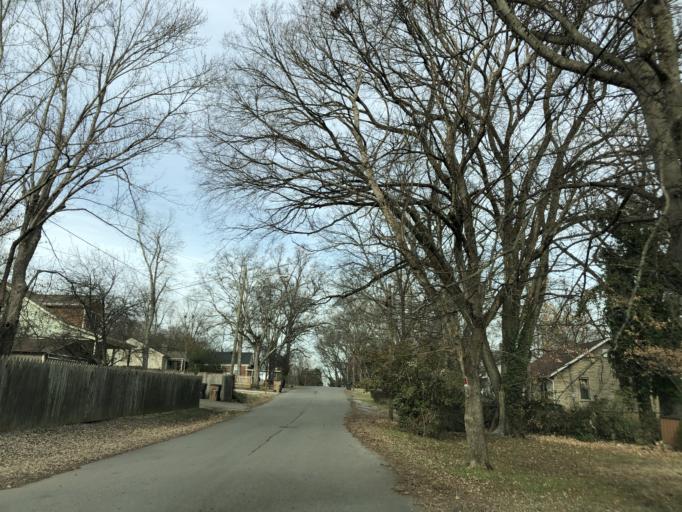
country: US
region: Tennessee
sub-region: Davidson County
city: Nashville
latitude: 36.2142
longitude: -86.7277
